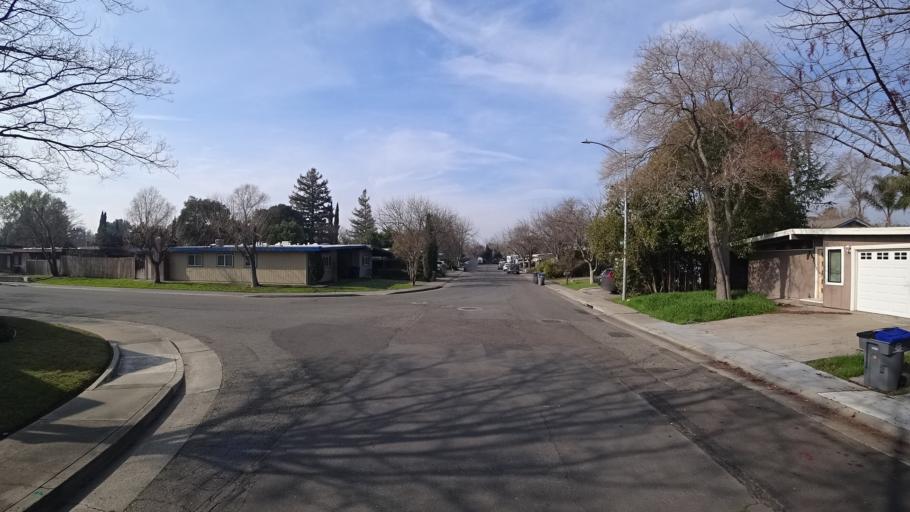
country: US
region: California
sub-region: Yolo County
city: Davis
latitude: 38.5696
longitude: -121.7566
